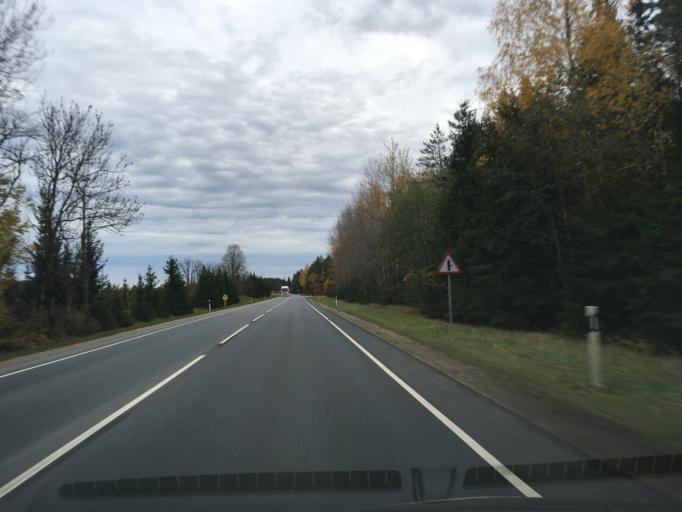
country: EE
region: Harju
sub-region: Nissi vald
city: Turba
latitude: 59.0328
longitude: 24.1602
